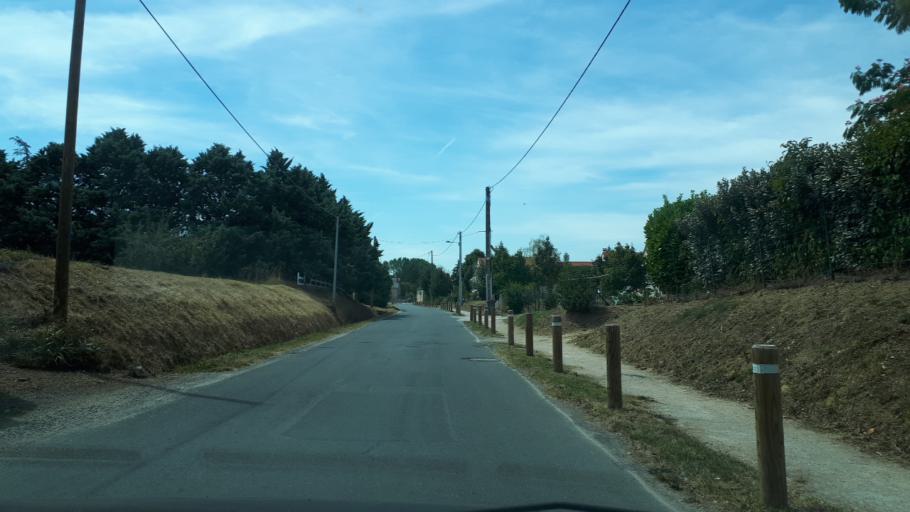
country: FR
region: Centre
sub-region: Departement du Loir-et-Cher
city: Contres
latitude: 47.3936
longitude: 1.3779
